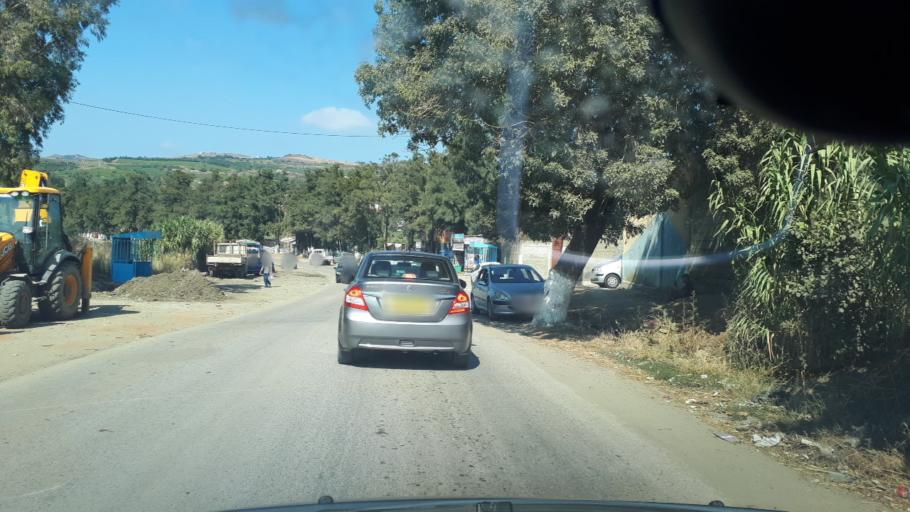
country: DZ
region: Boumerdes
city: Dellys
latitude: 36.8651
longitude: 3.8795
